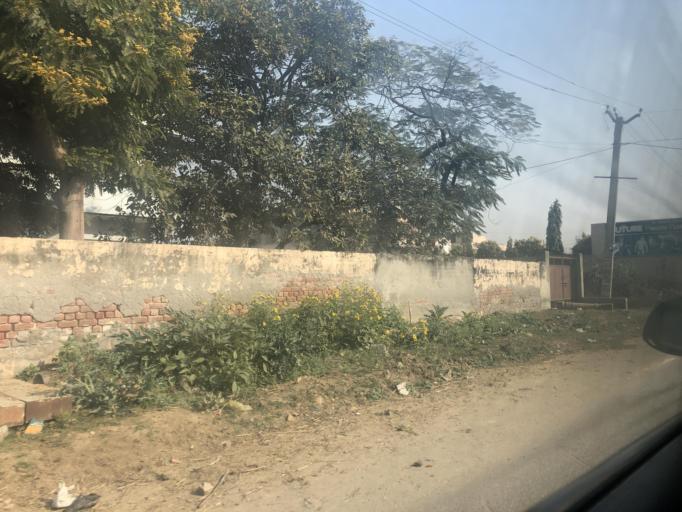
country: IN
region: Haryana
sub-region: Jhajjar
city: Bahadurgarh
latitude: 28.6866
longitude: 76.8961
